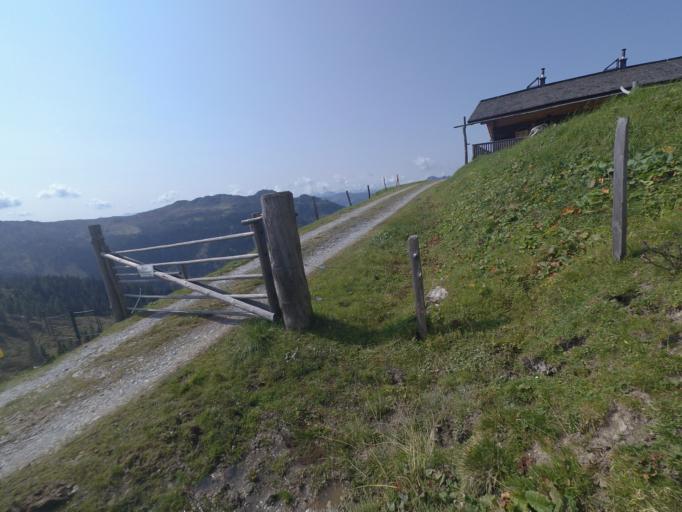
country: AT
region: Salzburg
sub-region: Politischer Bezirk Sankt Johann im Pongau
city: Kleinarl
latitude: 47.2763
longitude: 13.2713
